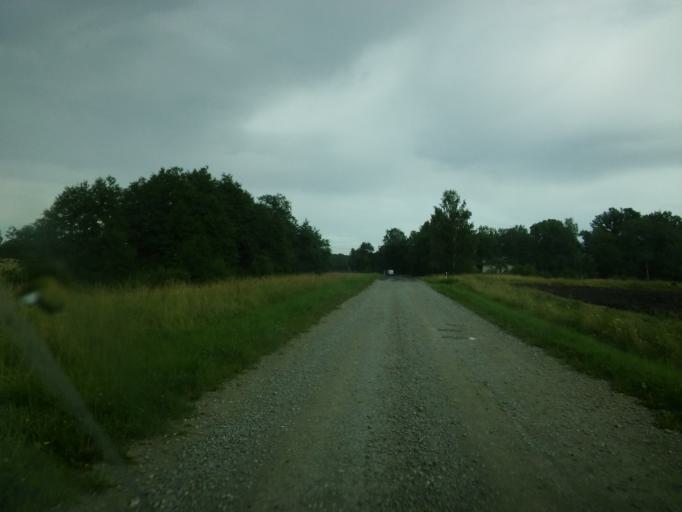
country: EE
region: Paernumaa
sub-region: Halinga vald
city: Parnu-Jaagupi
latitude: 58.7801
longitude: 24.5570
